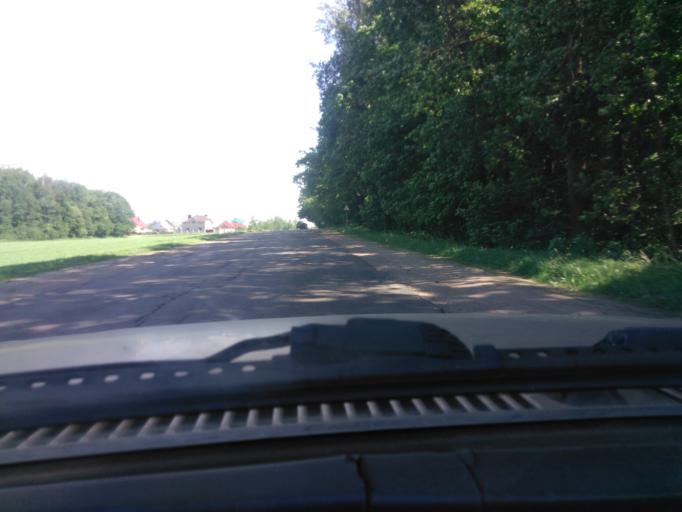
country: BY
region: Mogilev
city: Palykavichy Pyershyya
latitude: 53.9547
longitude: 30.3673
